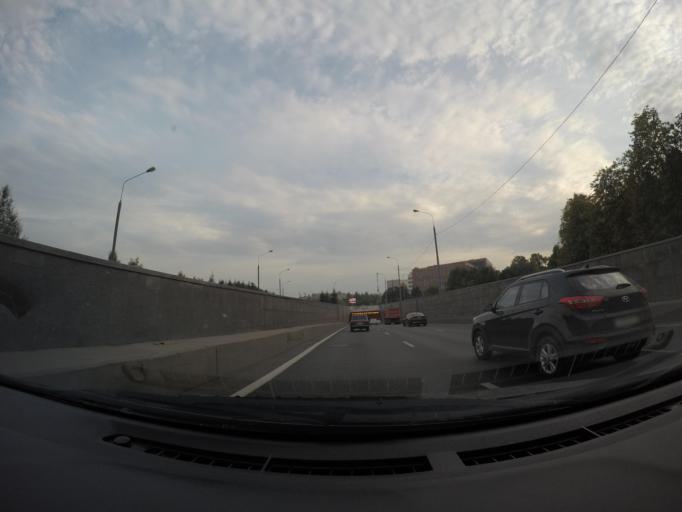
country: RU
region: Moscow
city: Tsaritsyno
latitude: 55.6548
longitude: 37.6530
